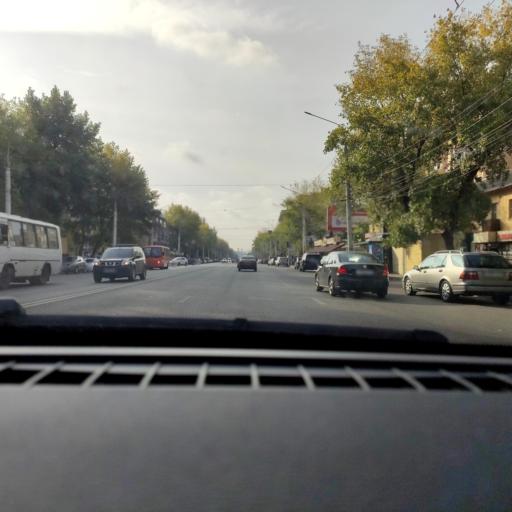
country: RU
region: Voronezj
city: Voronezh
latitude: 51.6445
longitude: 39.2381
